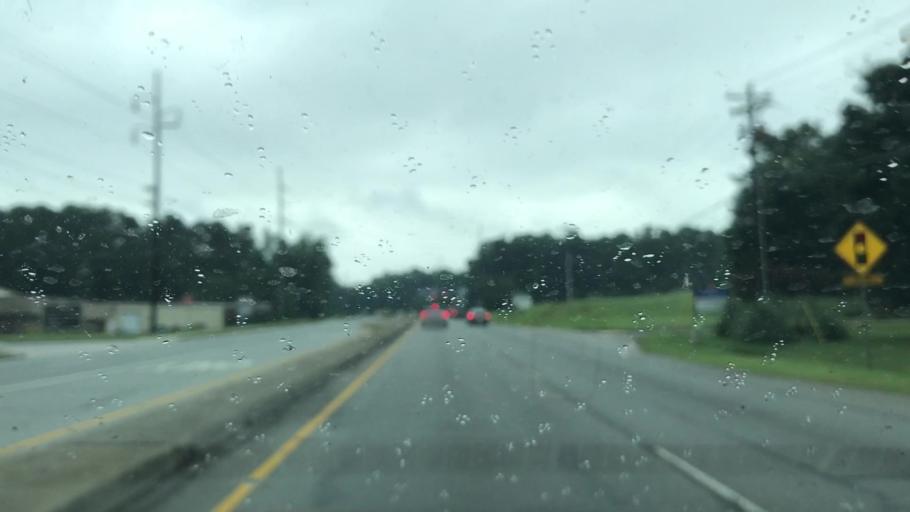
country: US
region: Georgia
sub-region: Gwinnett County
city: Lilburn
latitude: 33.9230
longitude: -84.1386
